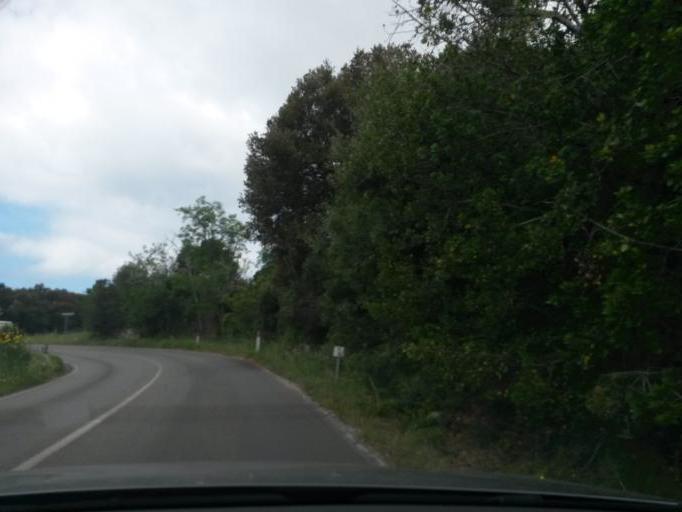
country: IT
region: Tuscany
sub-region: Provincia di Livorno
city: Marina di Campo
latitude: 42.7385
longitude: 10.2079
